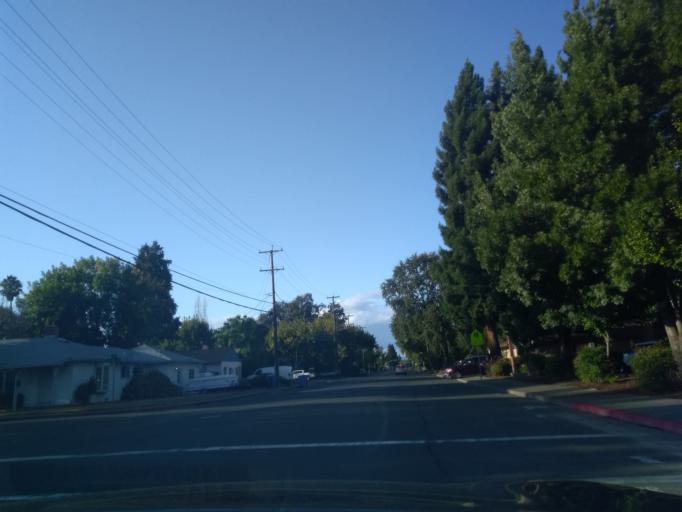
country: US
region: California
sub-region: Mendocino County
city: Ukiah
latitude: 39.1481
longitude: -123.1989
